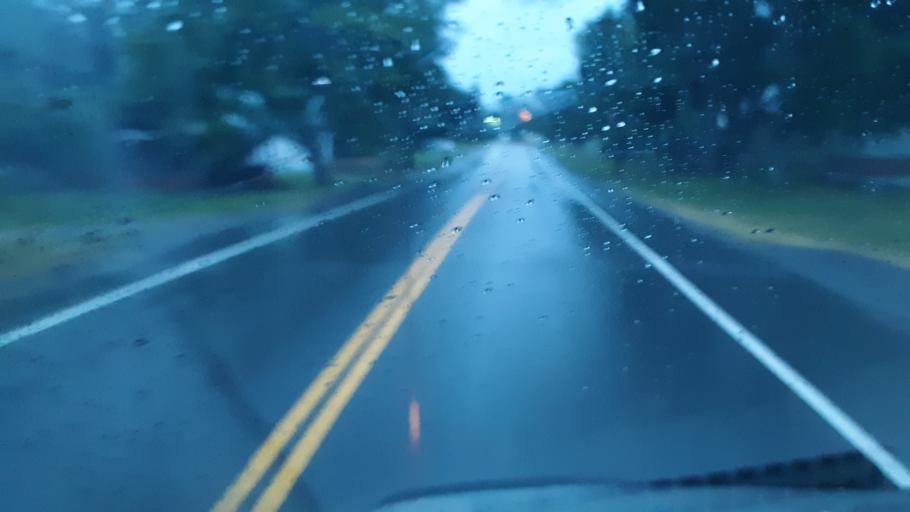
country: US
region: Maine
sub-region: Penobscot County
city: Patten
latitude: 45.9028
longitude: -68.4334
